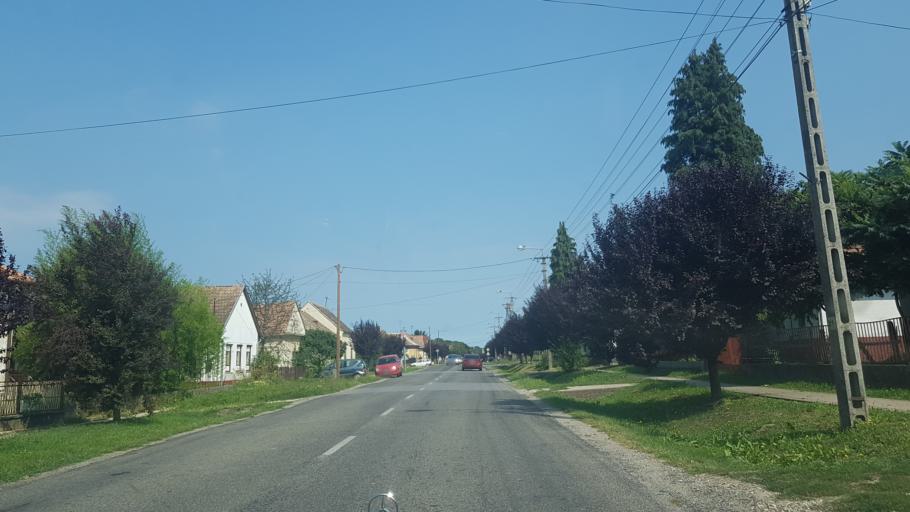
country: HU
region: Somogy
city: Segesd
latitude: 46.3466
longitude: 17.3464
